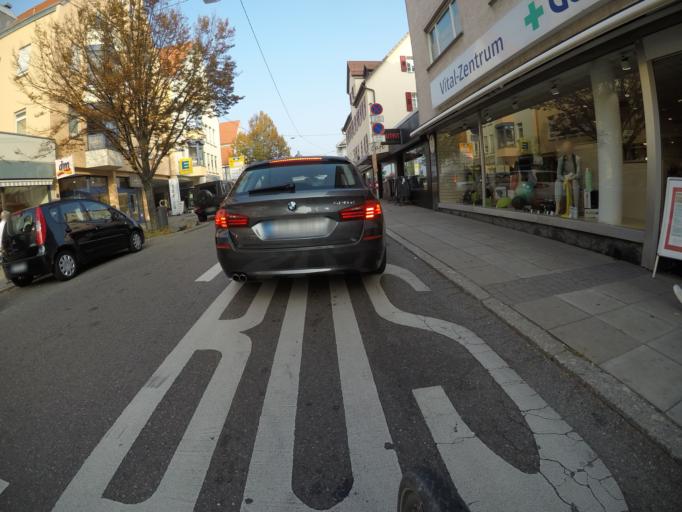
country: DE
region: Baden-Wuerttemberg
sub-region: Regierungsbezirk Stuttgart
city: Stuttgart
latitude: 48.7485
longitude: 9.1699
